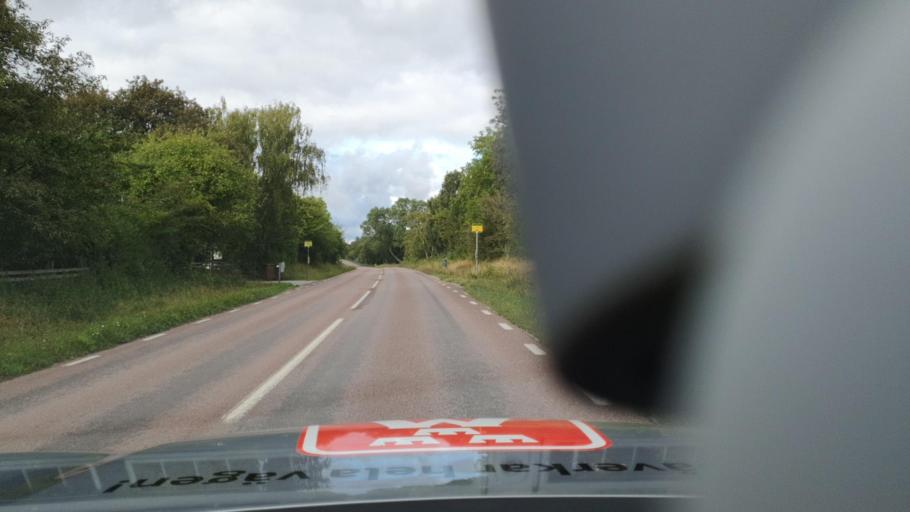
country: SE
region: Gotland
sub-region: Gotland
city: Hemse
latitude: 57.0461
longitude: 18.2905
